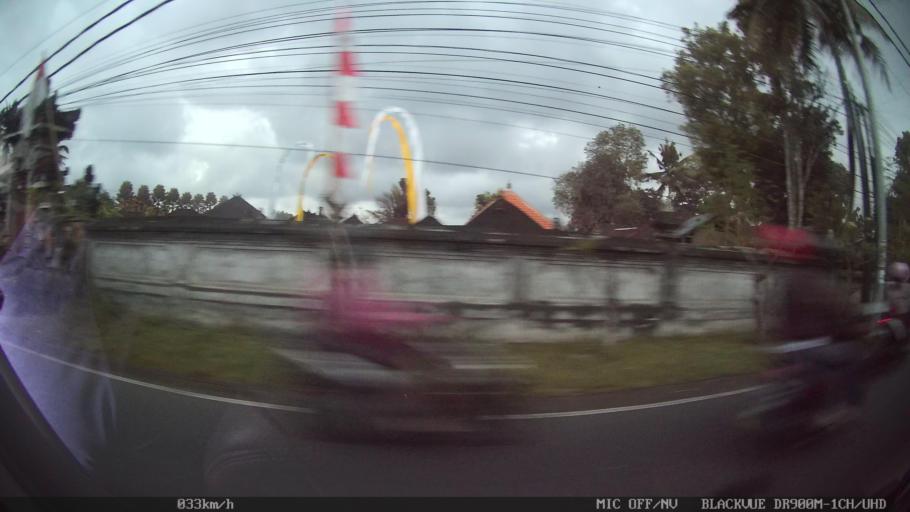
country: ID
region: Bali
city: Bunutan
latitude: -8.4635
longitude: 115.2473
